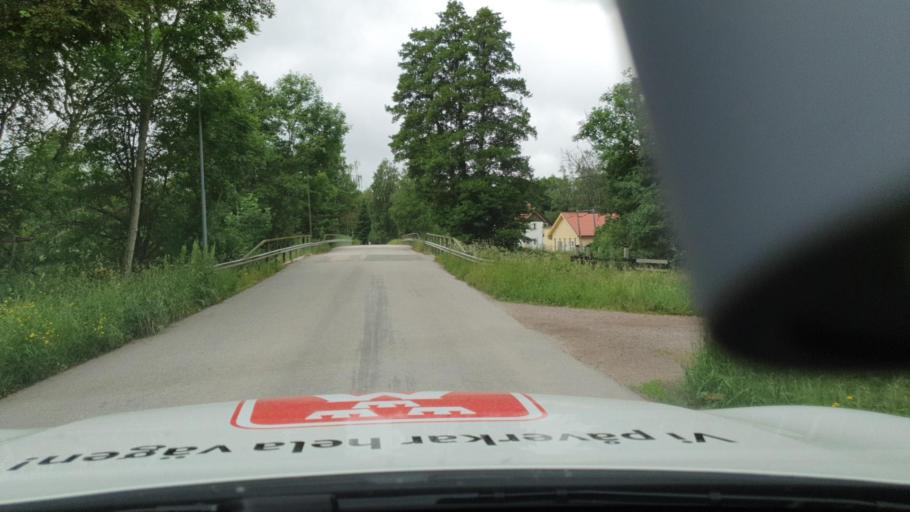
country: SE
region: Vaestra Goetaland
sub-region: Tibro Kommun
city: Tibro
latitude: 58.4046
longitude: 14.1385
